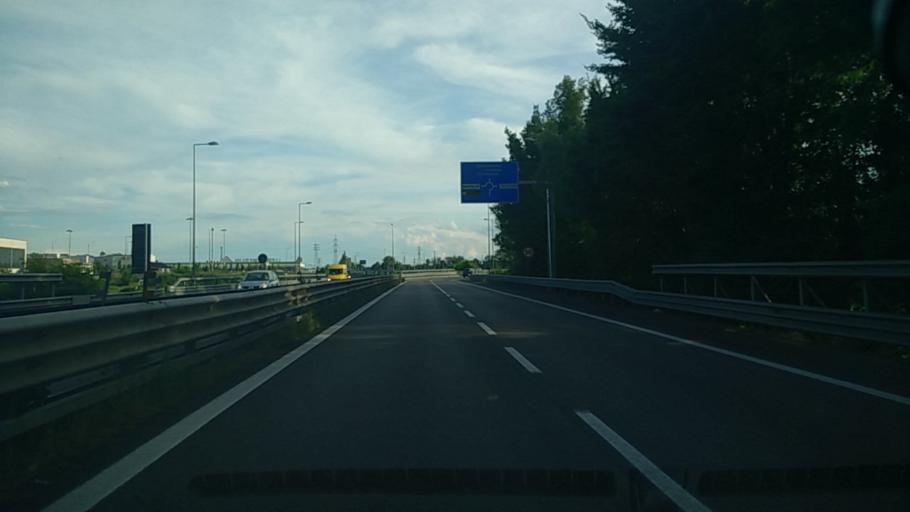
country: IT
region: Veneto
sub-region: Provincia di Venezia
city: Mestre
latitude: 45.4628
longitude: 12.2105
